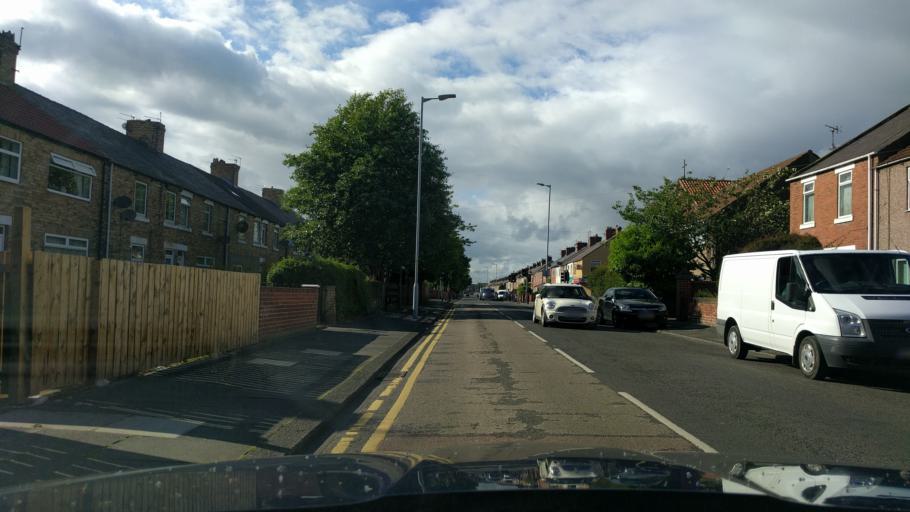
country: GB
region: England
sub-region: Northumberland
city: Ashington
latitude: 55.1792
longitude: -1.5608
